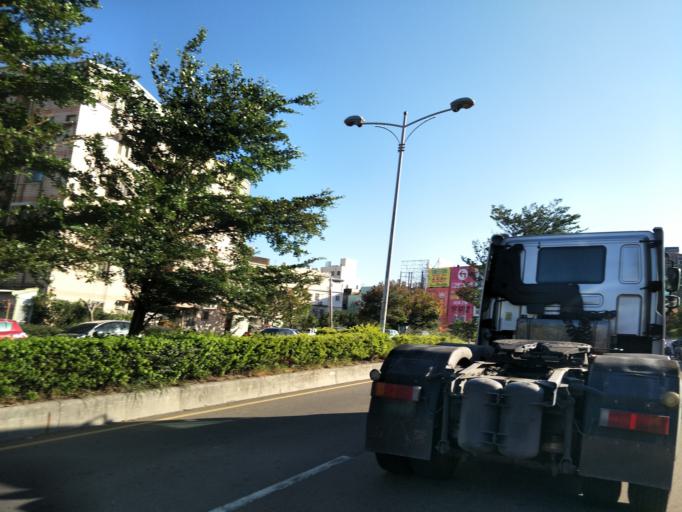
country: TW
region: Taiwan
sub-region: Hsinchu
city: Zhubei
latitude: 24.8371
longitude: 121.0209
